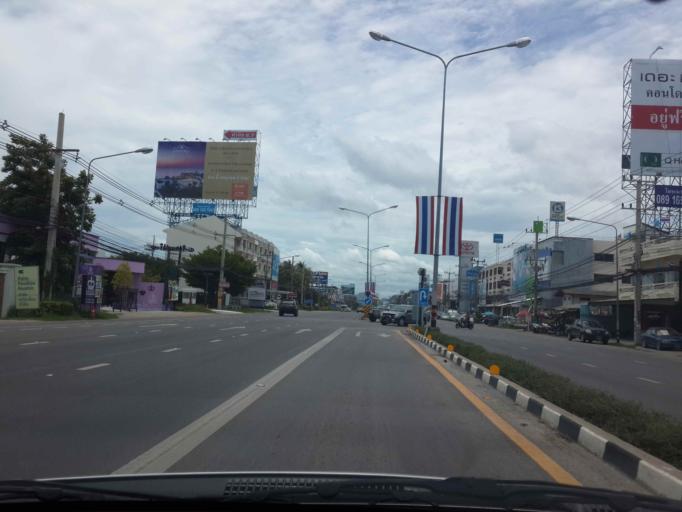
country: TH
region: Prachuap Khiri Khan
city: Hua Hin
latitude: 12.6193
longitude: 99.9506
